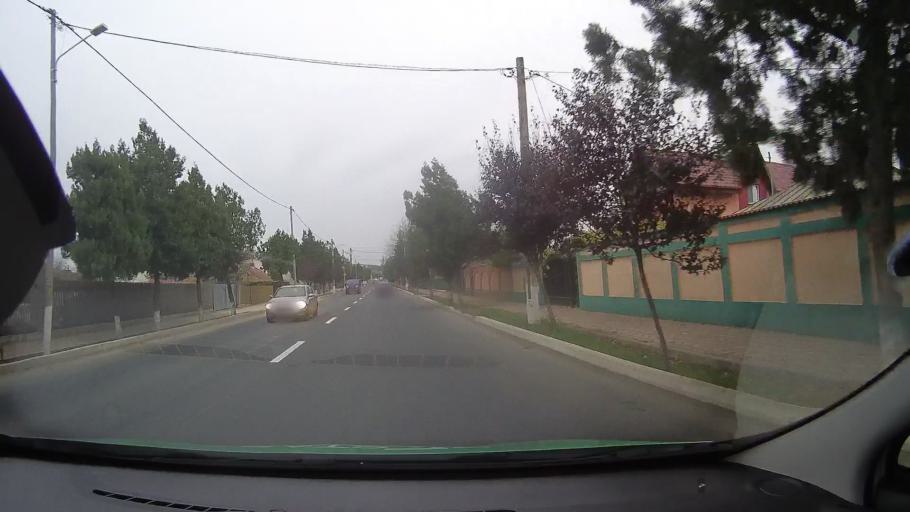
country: RO
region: Constanta
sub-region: Oras Harsova
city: Harsova
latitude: 44.6885
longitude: 27.9489
